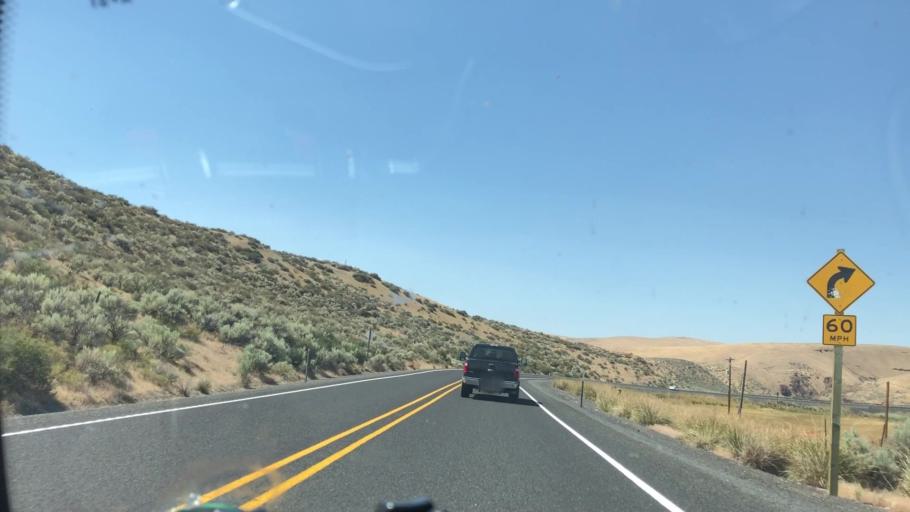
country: US
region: Idaho
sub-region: Owyhee County
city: Marsing
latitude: 43.2245
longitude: -117.0522
